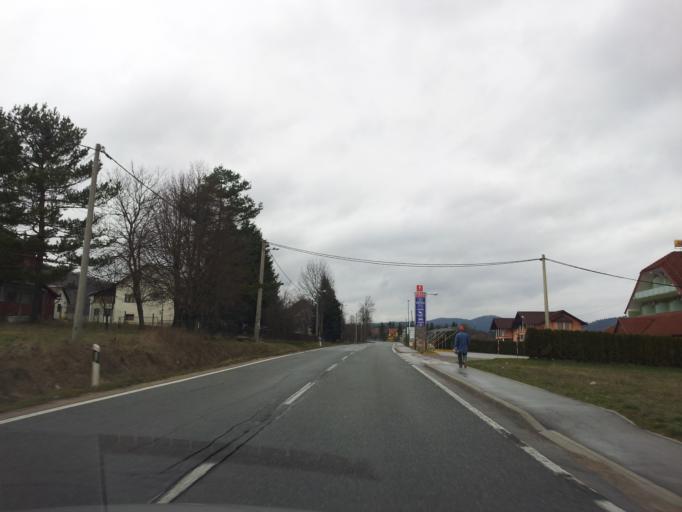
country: BA
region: Federation of Bosnia and Herzegovina
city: Izacic
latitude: 44.7570
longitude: 15.6978
